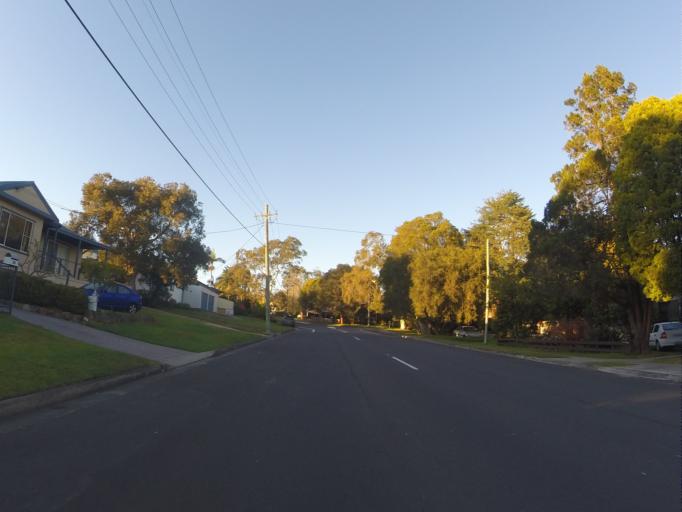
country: AU
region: New South Wales
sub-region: Sutherland Shire
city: Engadine
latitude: -34.0592
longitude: 151.0112
